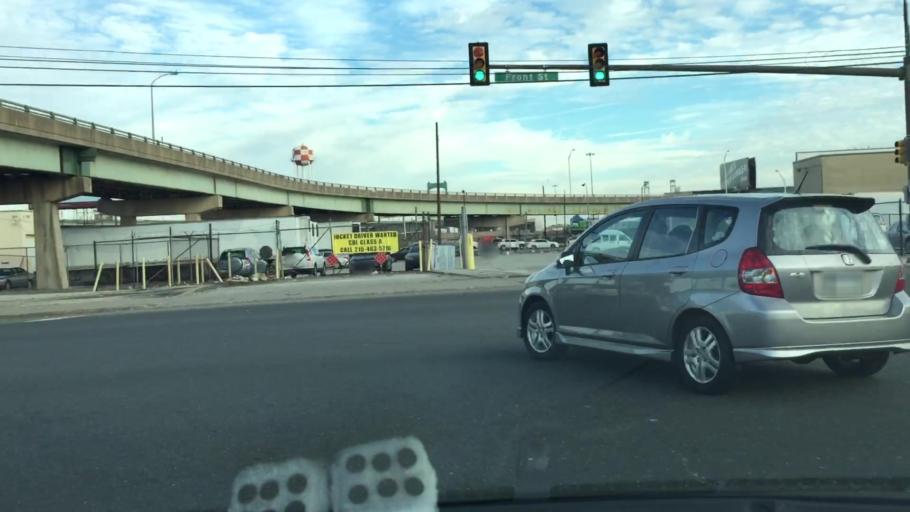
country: US
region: New Jersey
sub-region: Camden County
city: Camden
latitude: 39.9074
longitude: -75.1513
